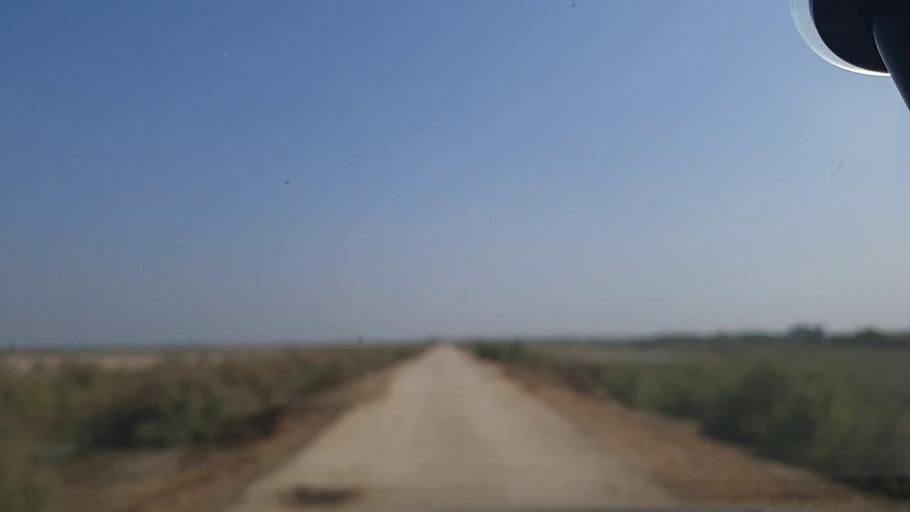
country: PK
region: Sindh
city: Chuhar Jamali
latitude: 24.4577
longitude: 67.8699
